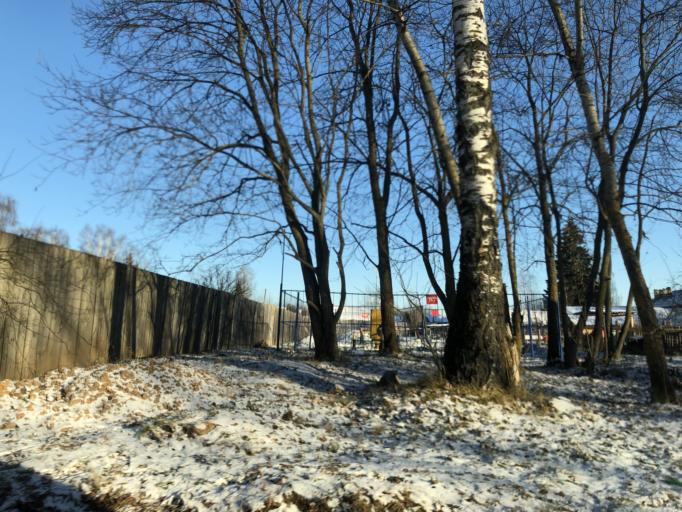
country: RU
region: Tverskaya
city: Rzhev
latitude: 56.2816
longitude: 34.3212
